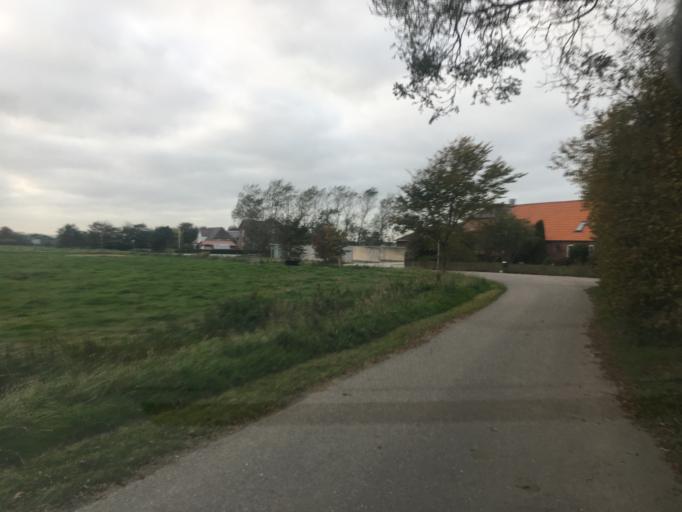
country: DE
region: Schleswig-Holstein
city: Rodenas
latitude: 54.9692
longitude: 8.7448
